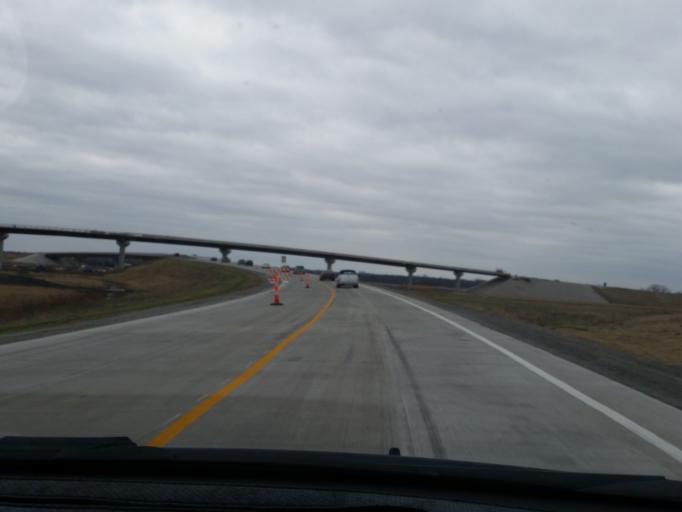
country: US
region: Kansas
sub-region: Douglas County
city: Lawrence
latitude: 38.9370
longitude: -95.1750
